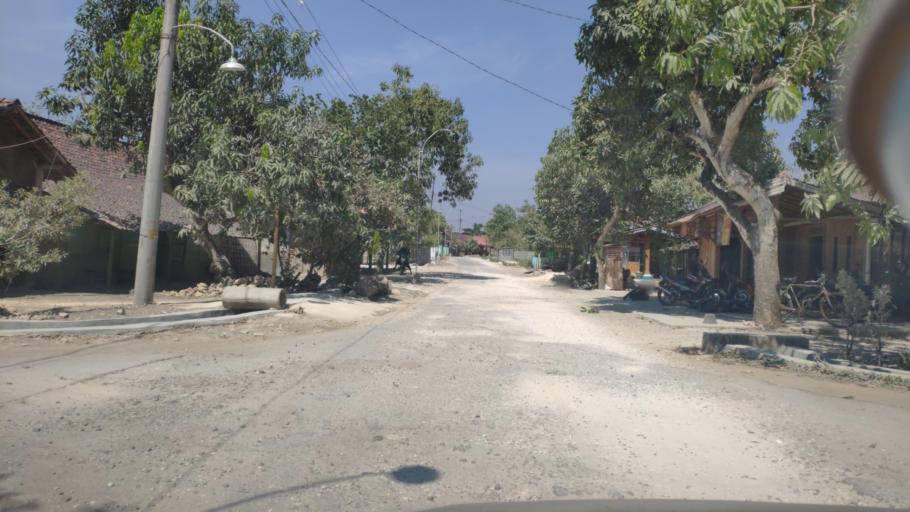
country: ID
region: Central Java
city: Kulonkali
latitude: -6.9943
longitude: 111.3771
